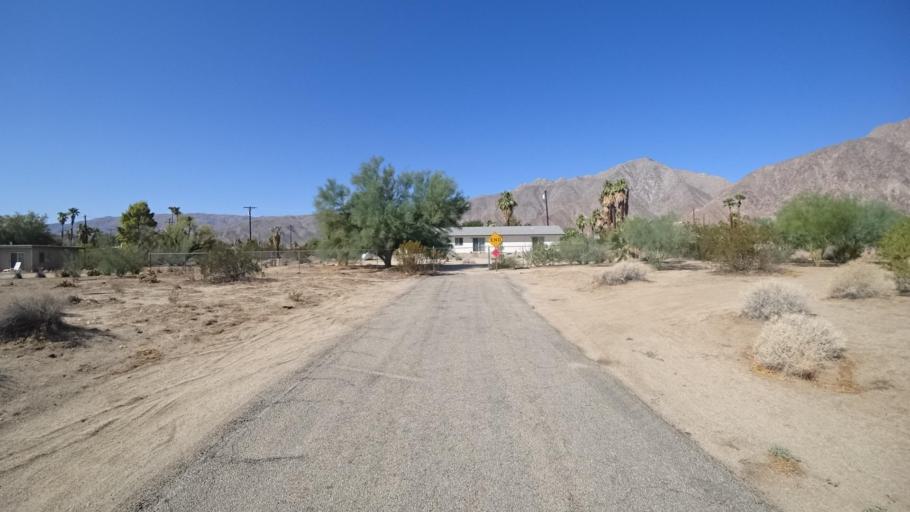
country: US
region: California
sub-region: San Diego County
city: Borrego Springs
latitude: 33.2746
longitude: -116.3907
